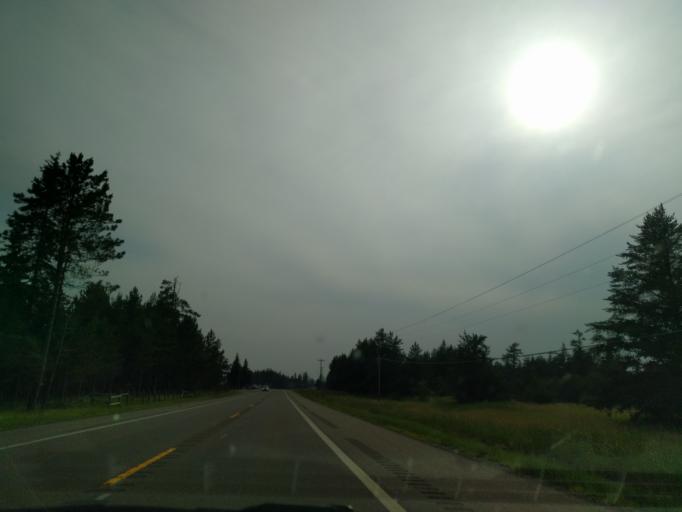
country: US
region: Michigan
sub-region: Marquette County
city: Gwinn
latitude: 46.2788
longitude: -87.3907
